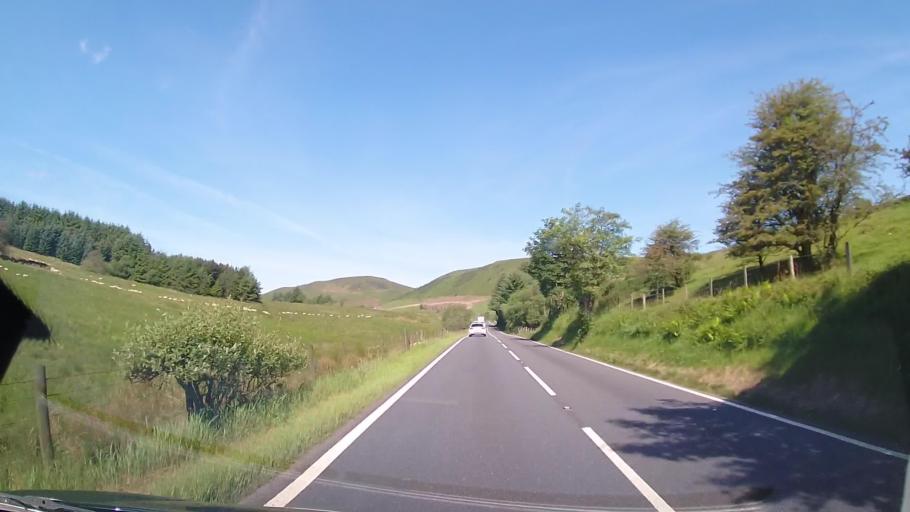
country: GB
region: Wales
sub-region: Gwynedd
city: Bala
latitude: 52.7103
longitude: -3.5682
